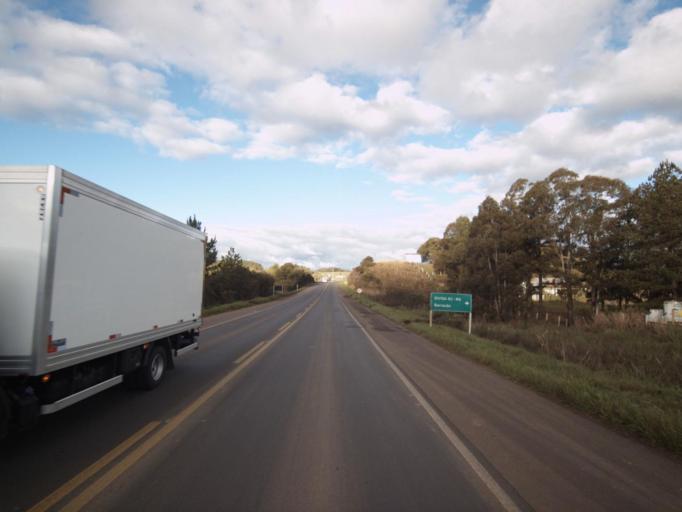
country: BR
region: Santa Catarina
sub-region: Campos Novos
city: Campos Novos
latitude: -27.3926
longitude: -51.1958
